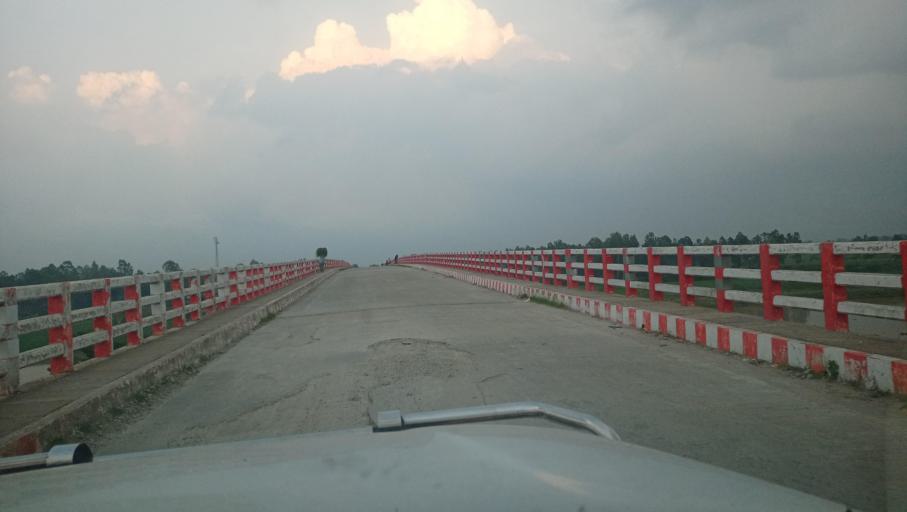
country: BD
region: Dhaka
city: Sherpur
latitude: 25.1766
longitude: 89.7904
